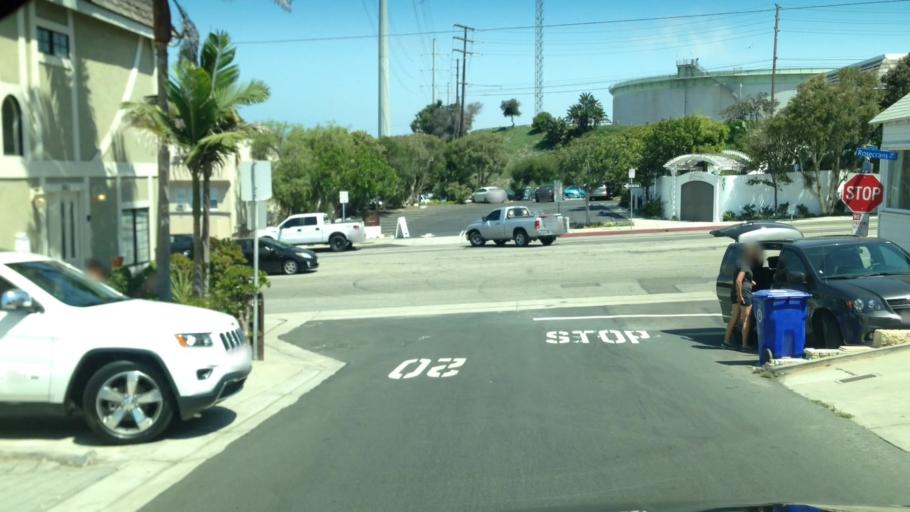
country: US
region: California
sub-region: Los Angeles County
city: Manhattan Beach
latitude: 33.9009
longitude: -118.4168
